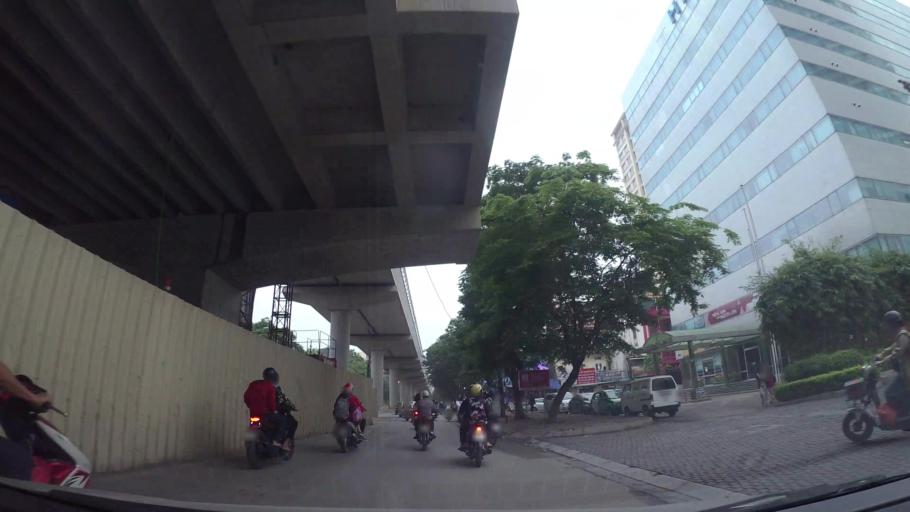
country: VN
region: Ha Noi
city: Cau Dien
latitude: 21.0365
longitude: 105.7830
